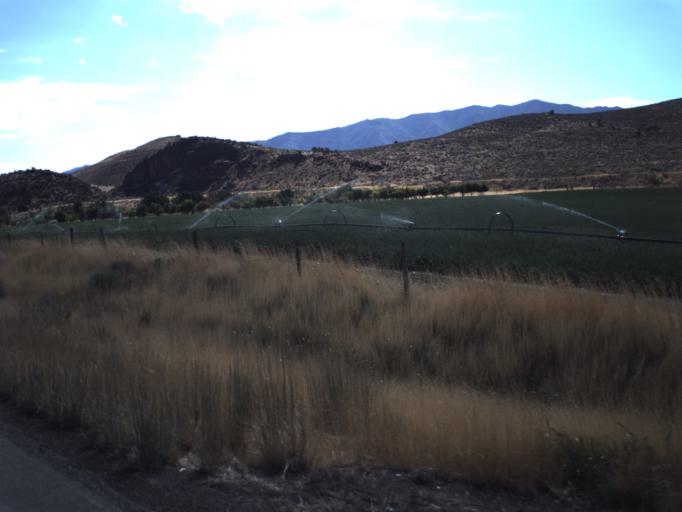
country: US
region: Utah
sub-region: Utah County
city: Genola
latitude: 39.9774
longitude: -111.8414
